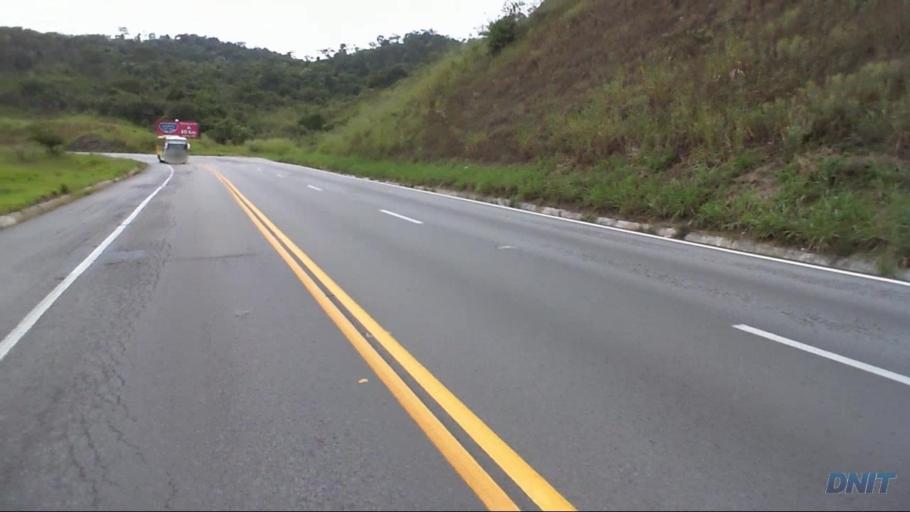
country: BR
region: Minas Gerais
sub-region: Nova Era
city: Nova Era
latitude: -19.6463
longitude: -42.9067
